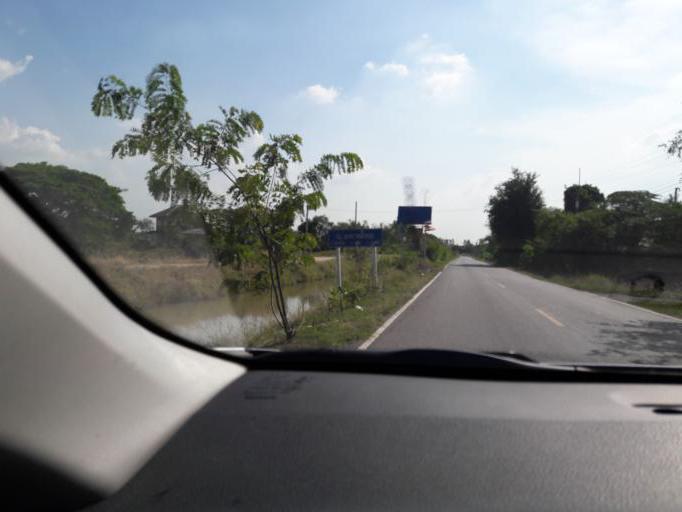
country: TH
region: Ang Thong
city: Ang Thong
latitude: 14.5782
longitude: 100.3956
